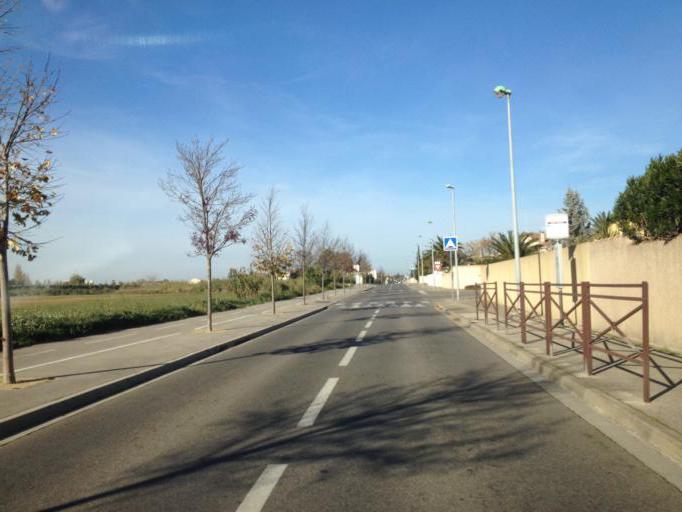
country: FR
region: Provence-Alpes-Cote d'Azur
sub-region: Departement des Bouches-du-Rhone
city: Istres
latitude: 43.5068
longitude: 4.9677
